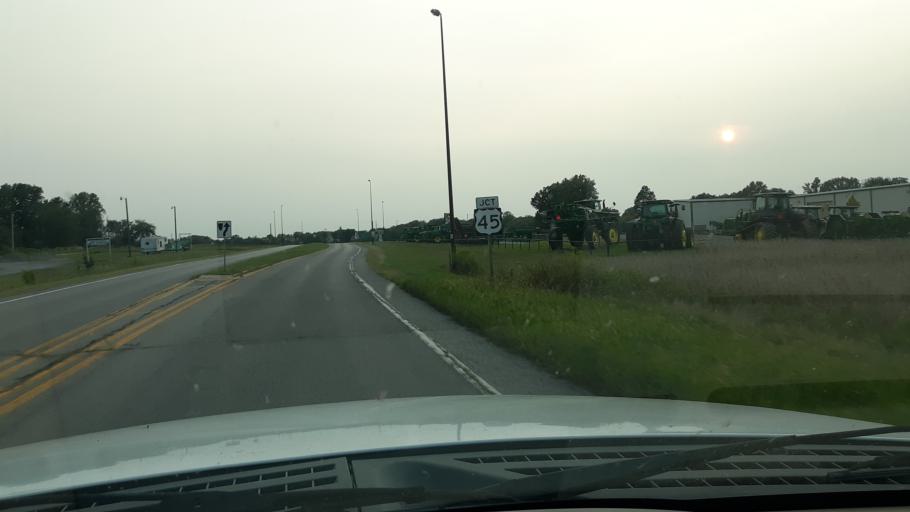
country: US
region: Illinois
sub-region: White County
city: Norris City
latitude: 37.9673
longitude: -88.3256
